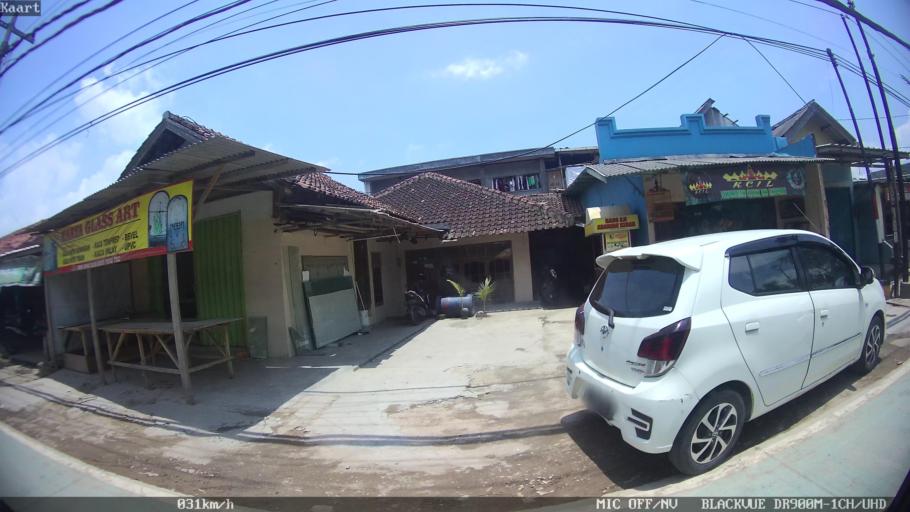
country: ID
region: Lampung
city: Kedaton
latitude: -5.3803
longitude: 105.2900
